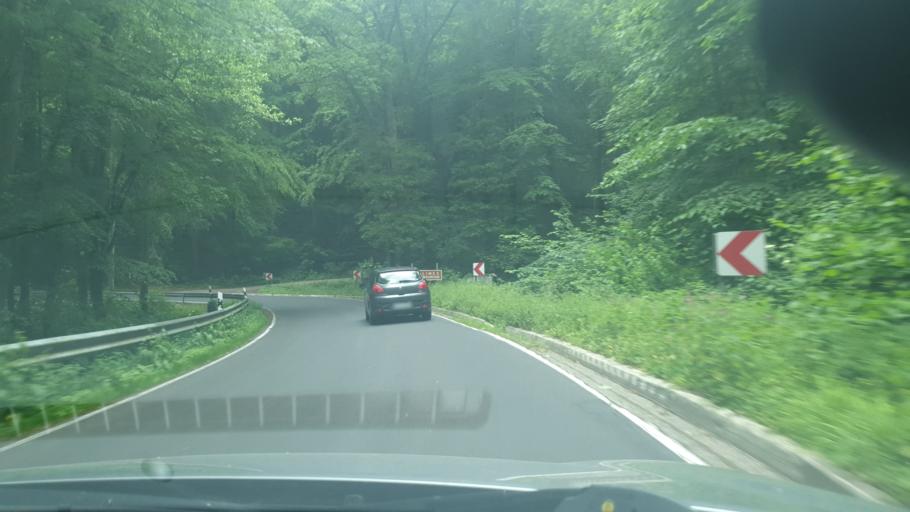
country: DE
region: Rheinland-Pfalz
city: Neuhausel
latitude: 50.3999
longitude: 7.7186
